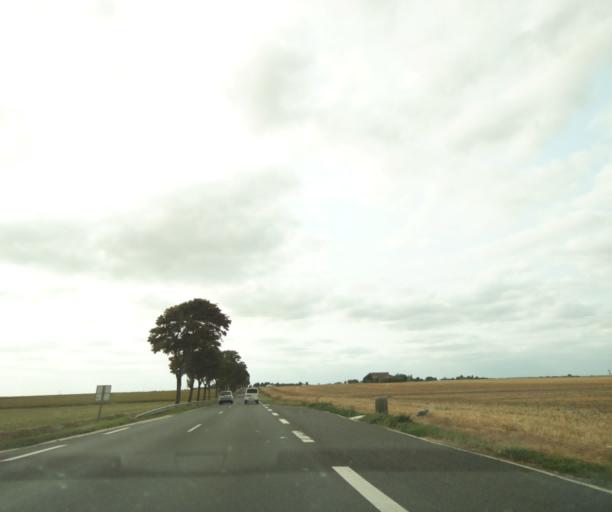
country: FR
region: Centre
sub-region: Departement d'Indre-et-Loire
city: Chambourg-sur-Indre
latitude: 47.1911
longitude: 0.9313
